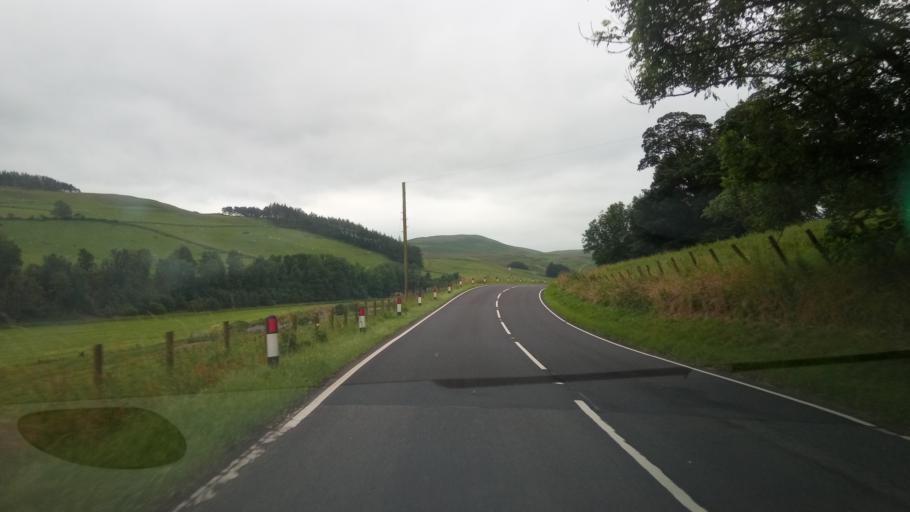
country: GB
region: Scotland
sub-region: The Scottish Borders
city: Hawick
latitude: 55.3679
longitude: -2.8807
